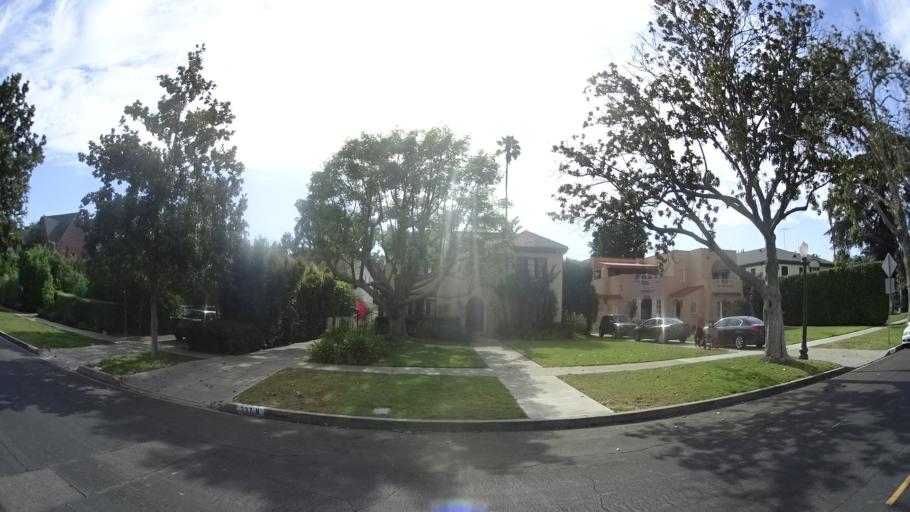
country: US
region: California
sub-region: Los Angeles County
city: Hollywood
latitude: 34.0756
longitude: -118.3171
